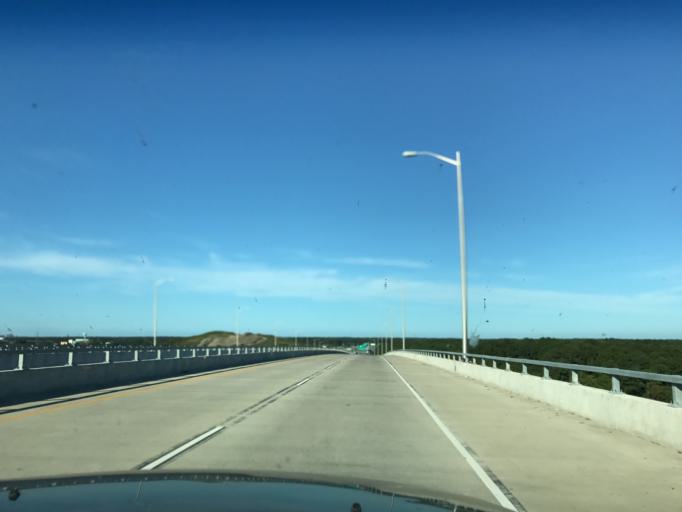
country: US
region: Virginia
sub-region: City of Chesapeake
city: Chesapeake
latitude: 36.7369
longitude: -76.2941
